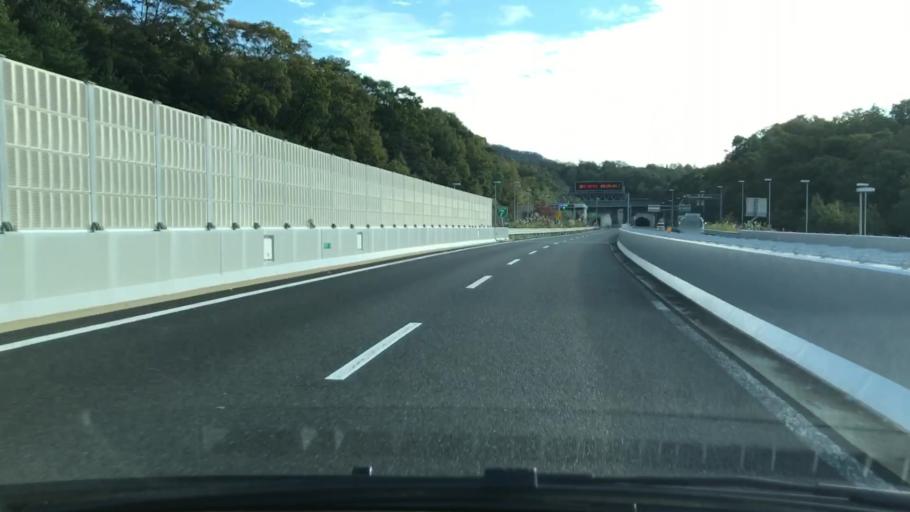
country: JP
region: Hyogo
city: Sandacho
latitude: 34.8184
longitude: 135.2509
